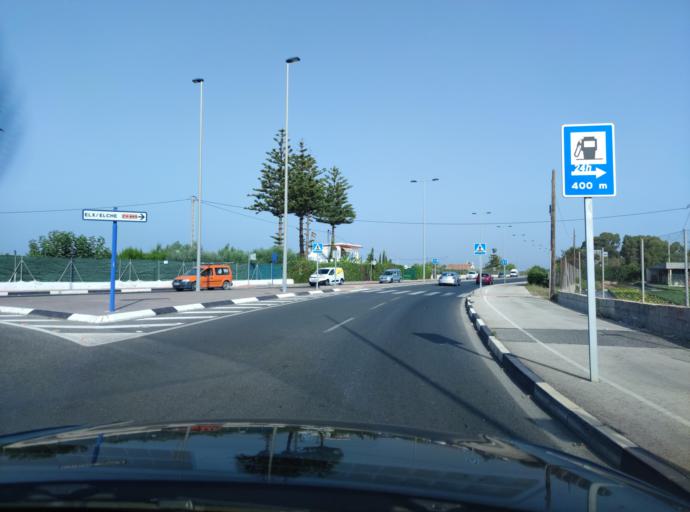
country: ES
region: Valencia
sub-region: Provincia de Alicante
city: Santa Pola
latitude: 38.2055
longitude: -0.5800
